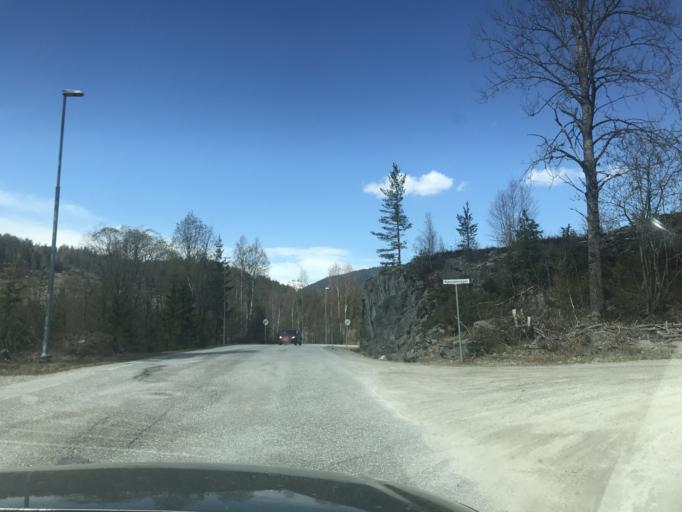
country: NO
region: Telemark
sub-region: Hjartdal
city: Sauland
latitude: 59.7186
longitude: 8.8504
